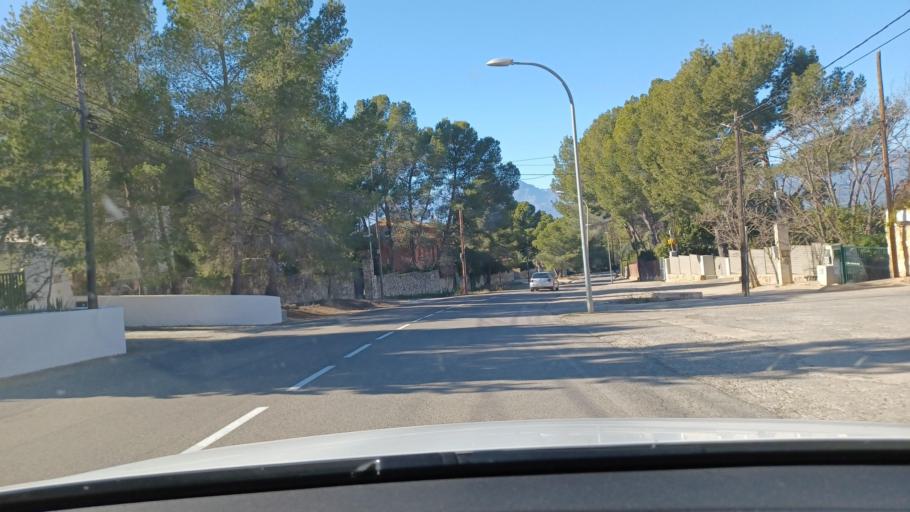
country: ES
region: Catalonia
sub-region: Provincia de Tarragona
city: Tortosa
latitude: 40.8132
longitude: 0.5428
